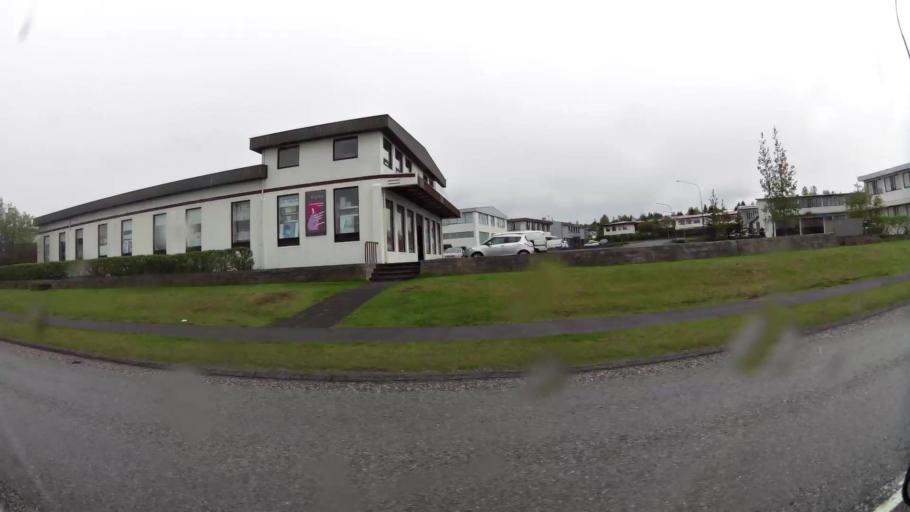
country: IS
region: Capital Region
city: Gardabaer
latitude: 64.0927
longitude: -21.9026
